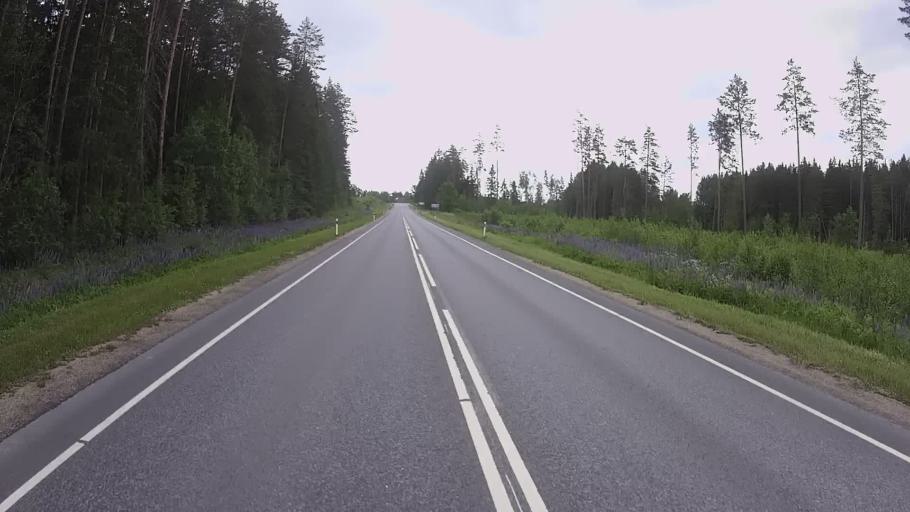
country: EE
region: Polvamaa
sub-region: Polva linn
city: Polva
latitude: 58.0982
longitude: 27.0004
